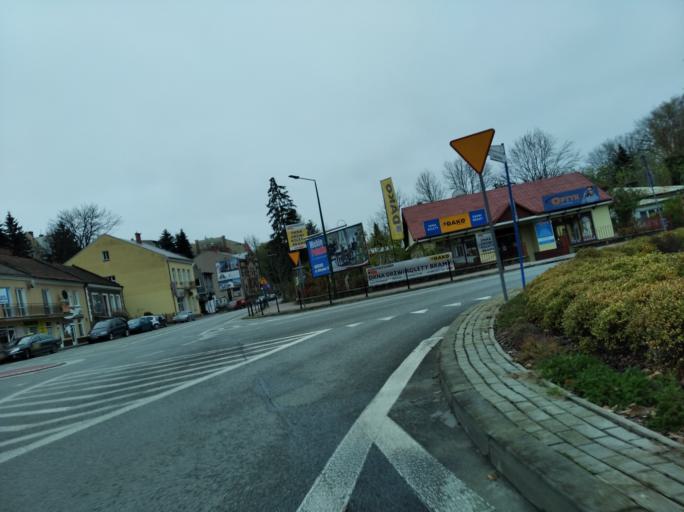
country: PL
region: Subcarpathian Voivodeship
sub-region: Krosno
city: Krosno
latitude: 49.6944
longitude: 21.7625
